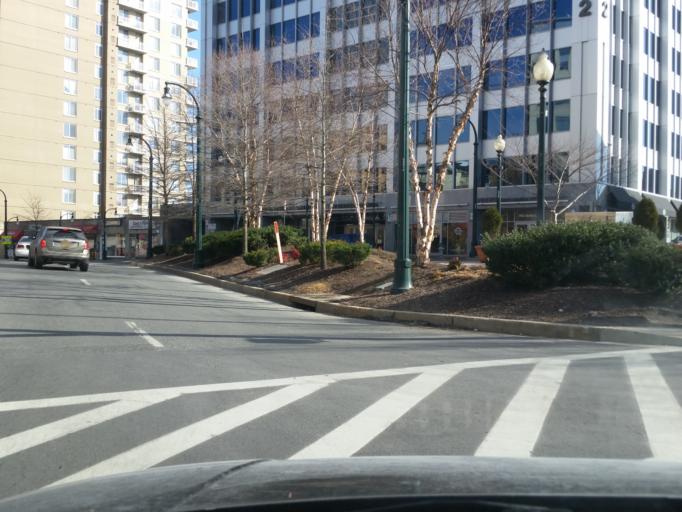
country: US
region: Maryland
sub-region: Montgomery County
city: Silver Spring
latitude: 38.9945
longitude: -77.0267
